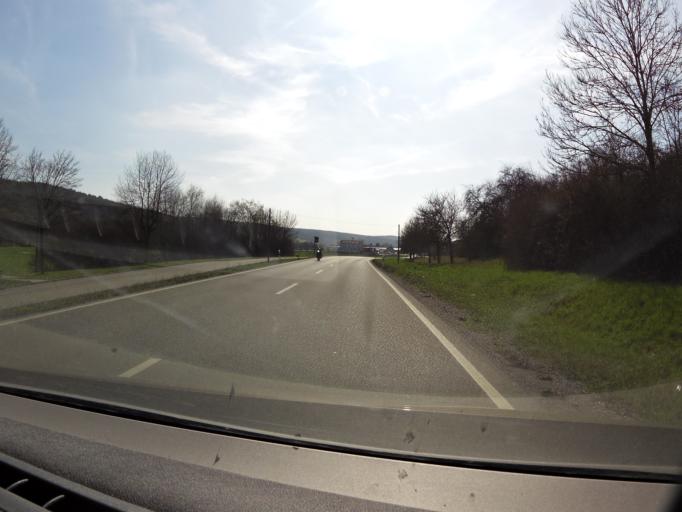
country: DE
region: Bavaria
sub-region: Regierungsbezirk Unterfranken
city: Rottingen
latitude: 49.5163
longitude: 9.9827
